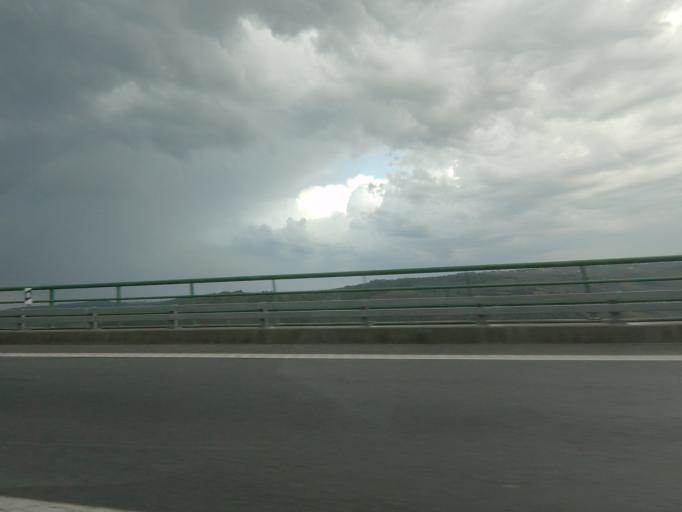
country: PT
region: Vila Real
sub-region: Santa Marta de Penaguiao
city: Santa Marta de Penaguiao
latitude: 41.2096
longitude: -7.7369
